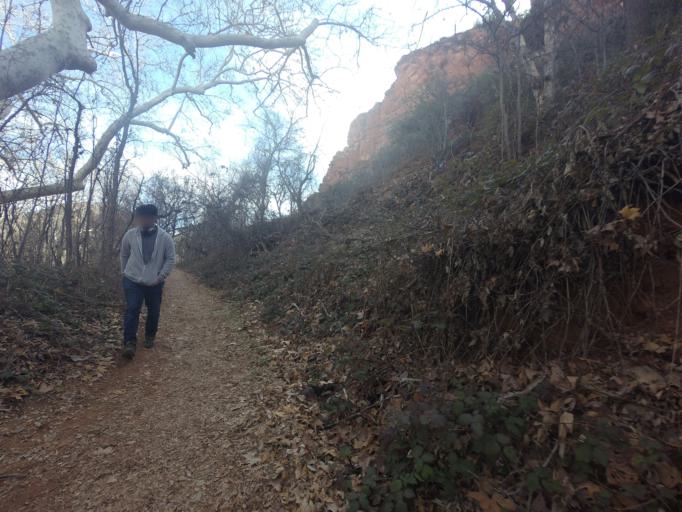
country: US
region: Arizona
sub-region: Yavapai County
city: West Sedona
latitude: 34.8112
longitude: -111.8317
